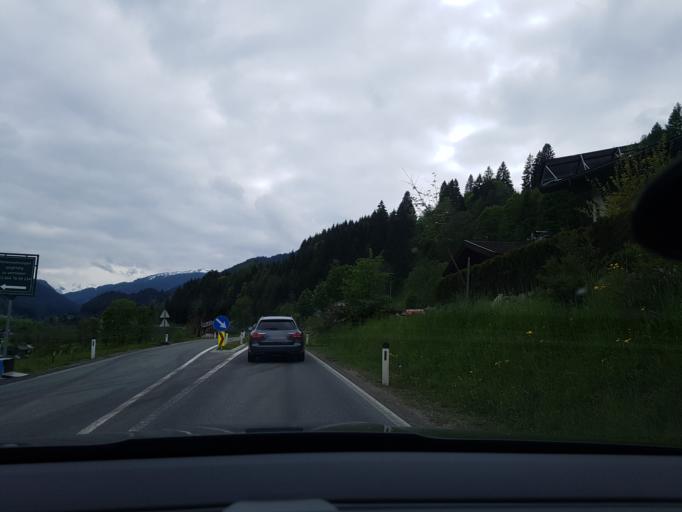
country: AT
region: Tyrol
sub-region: Politischer Bezirk Kitzbuhel
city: Jochberg
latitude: 47.3715
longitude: 12.4180
